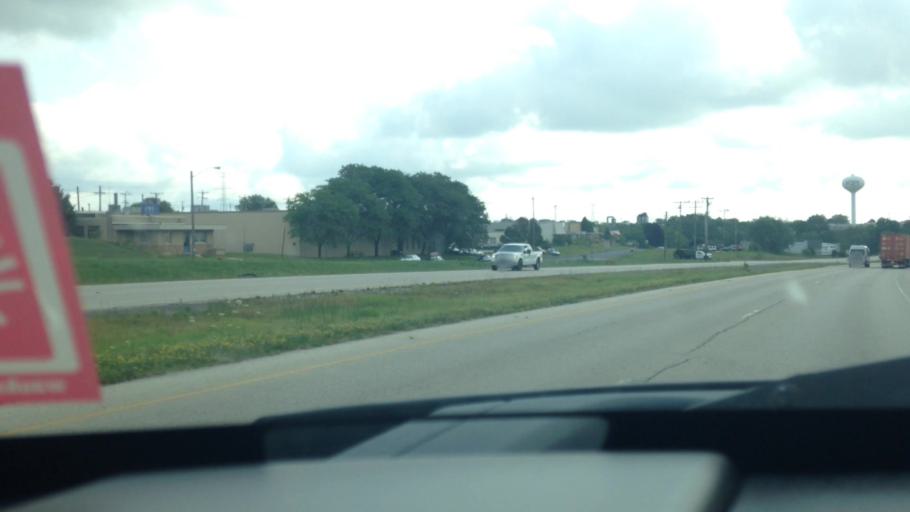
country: US
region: Wisconsin
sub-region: Waukesha County
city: Butler
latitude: 43.1187
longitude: -88.0819
